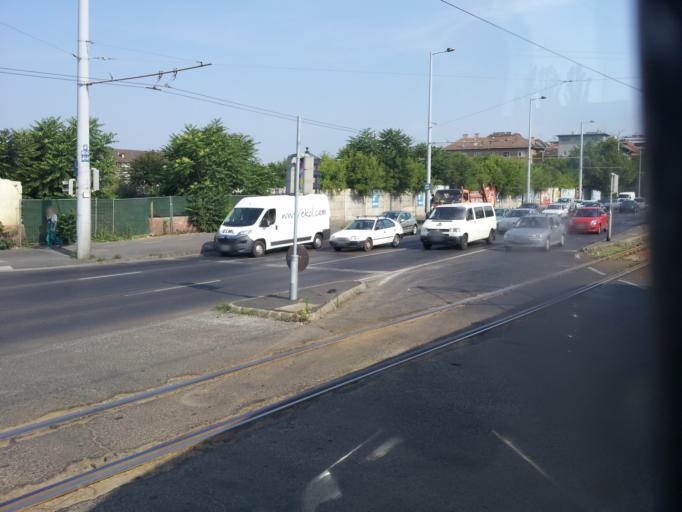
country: HU
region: Budapest
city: Budapest XIV. keruelet
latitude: 47.4964
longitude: 19.1091
